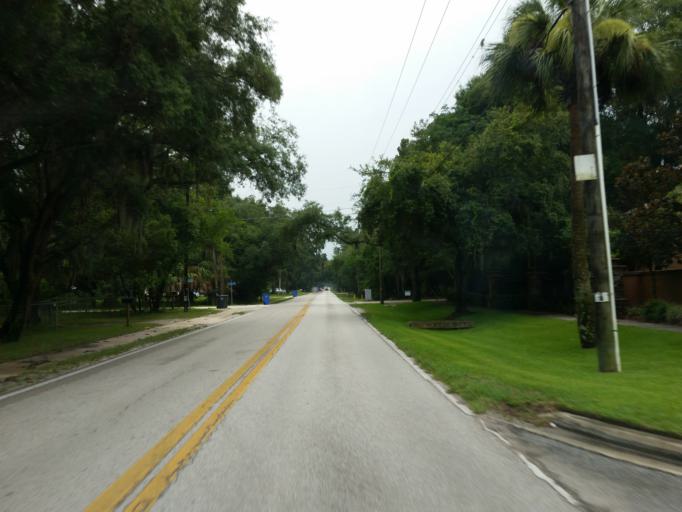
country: US
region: Florida
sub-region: Hillsborough County
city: Bloomingdale
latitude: 27.8905
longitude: -82.2858
